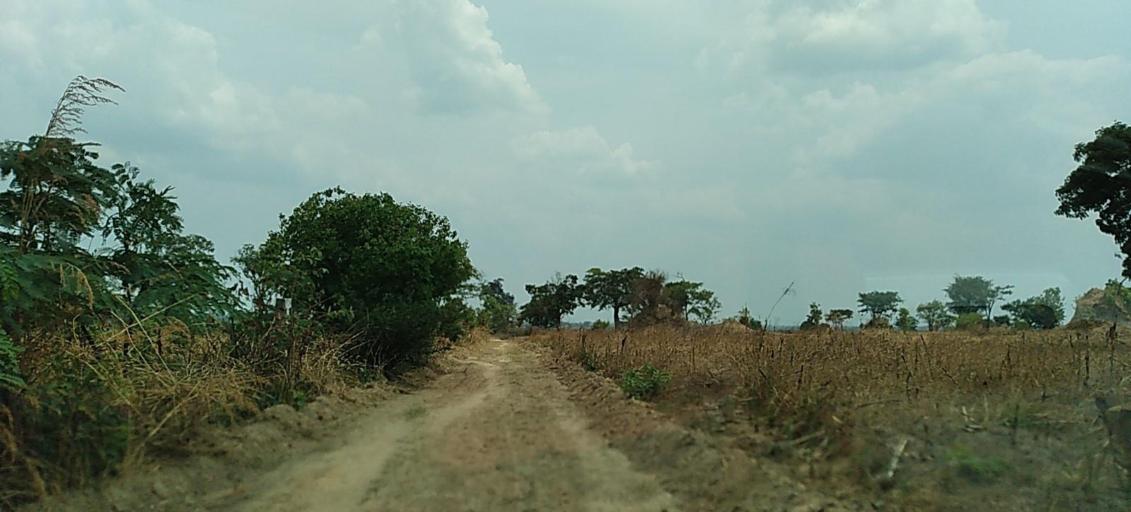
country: ZM
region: Copperbelt
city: Chililabombwe
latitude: -12.3564
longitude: 27.7994
